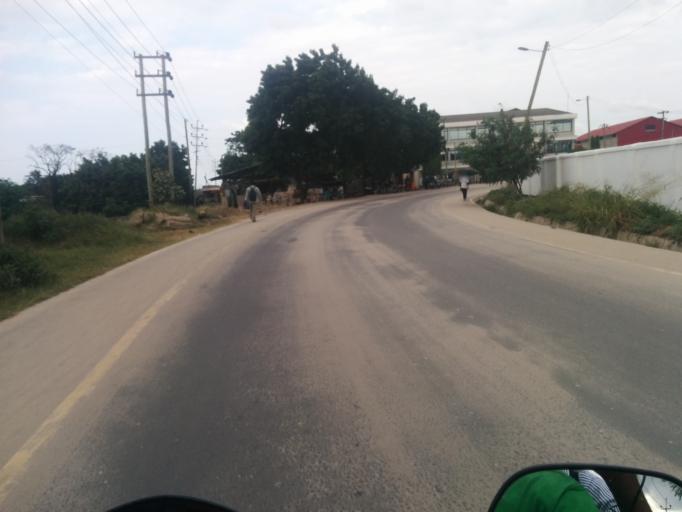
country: TZ
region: Dar es Salaam
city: Dar es Salaam
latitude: -6.8302
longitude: 39.2751
